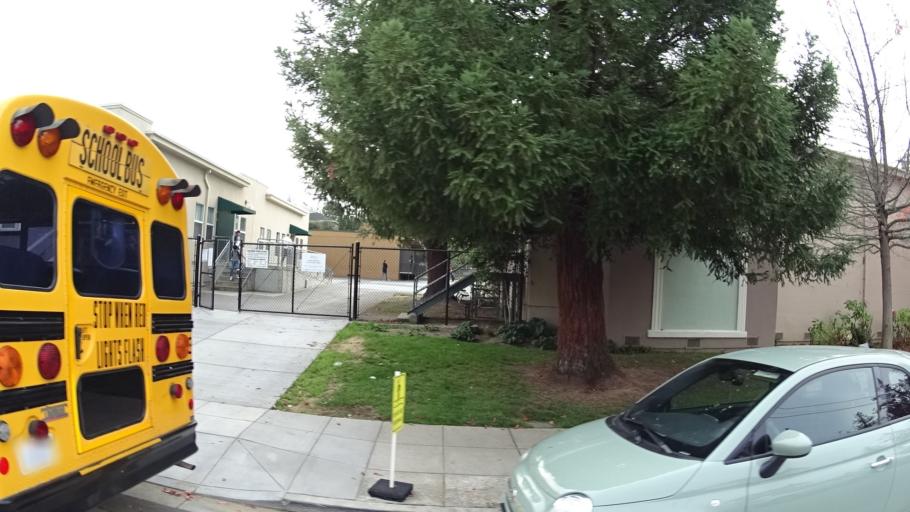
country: US
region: California
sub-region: San Mateo County
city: Burlingame
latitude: 37.5797
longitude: -122.3691
